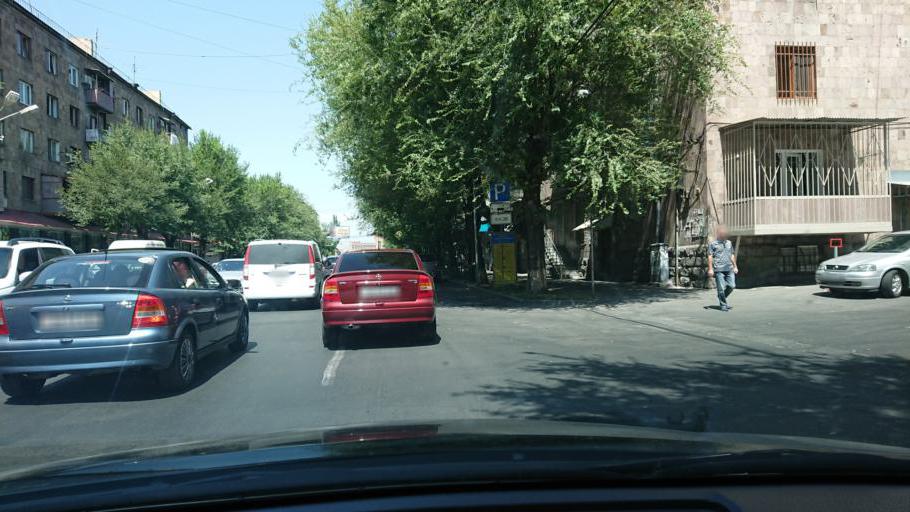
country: AM
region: Yerevan
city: Yerevan
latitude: 40.2038
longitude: 44.4981
